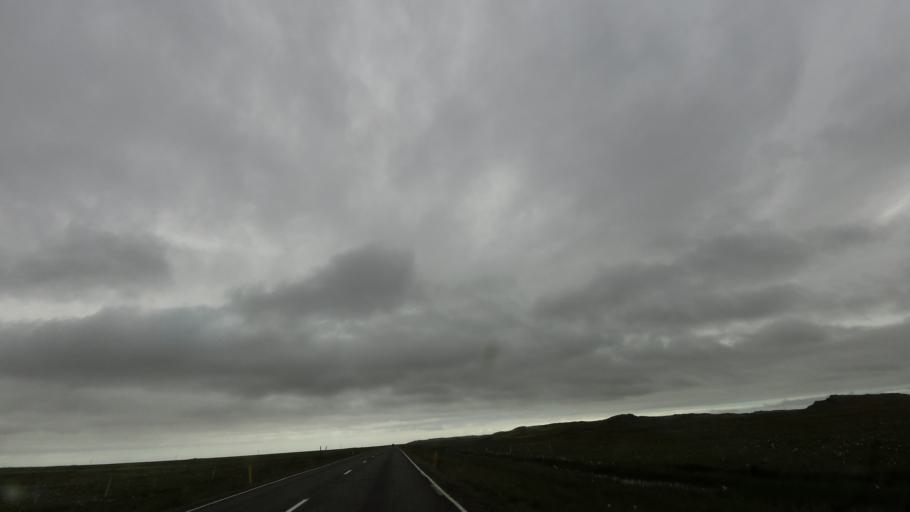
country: IS
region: East
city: Hoefn
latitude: 64.3247
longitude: -15.4162
